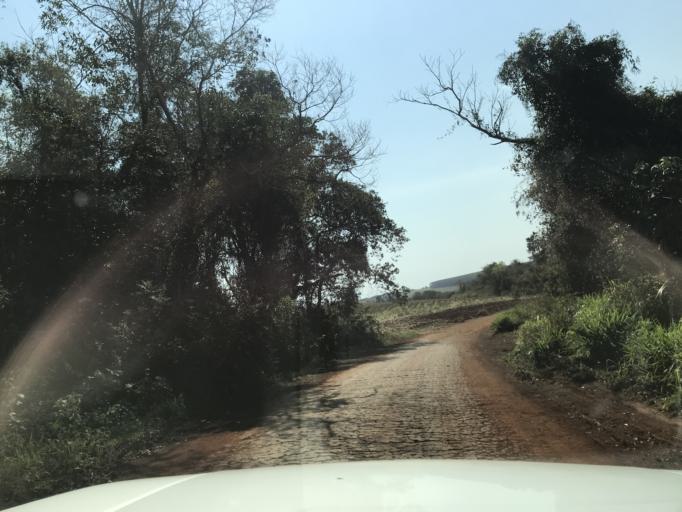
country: BR
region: Parana
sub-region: Palotina
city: Palotina
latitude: -24.2197
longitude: -53.7349
